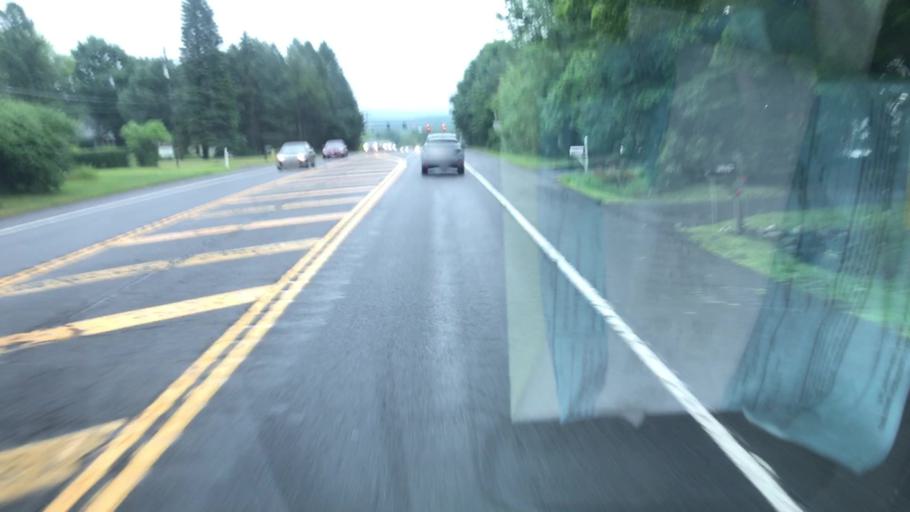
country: US
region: New York
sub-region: Onondaga County
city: Fayetteville
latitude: 43.0164
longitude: -76.0177
